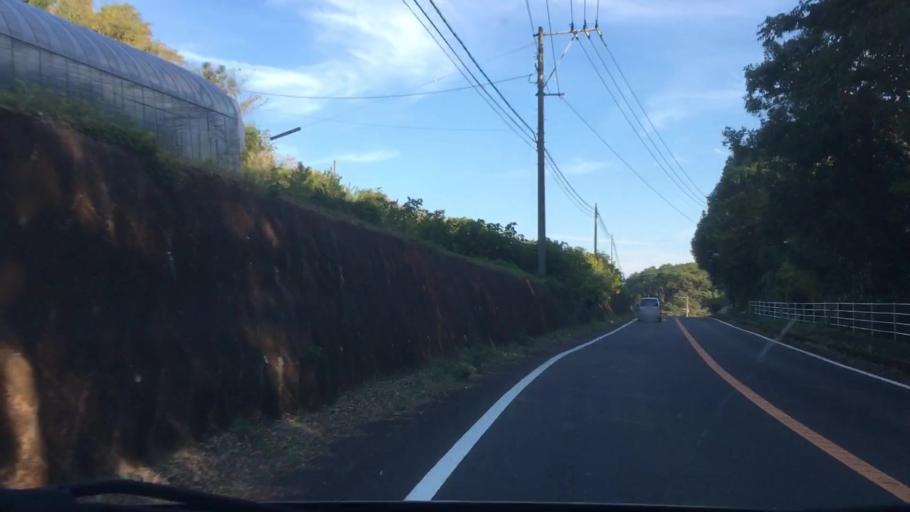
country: JP
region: Nagasaki
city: Sasebo
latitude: 33.0453
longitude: 129.7003
